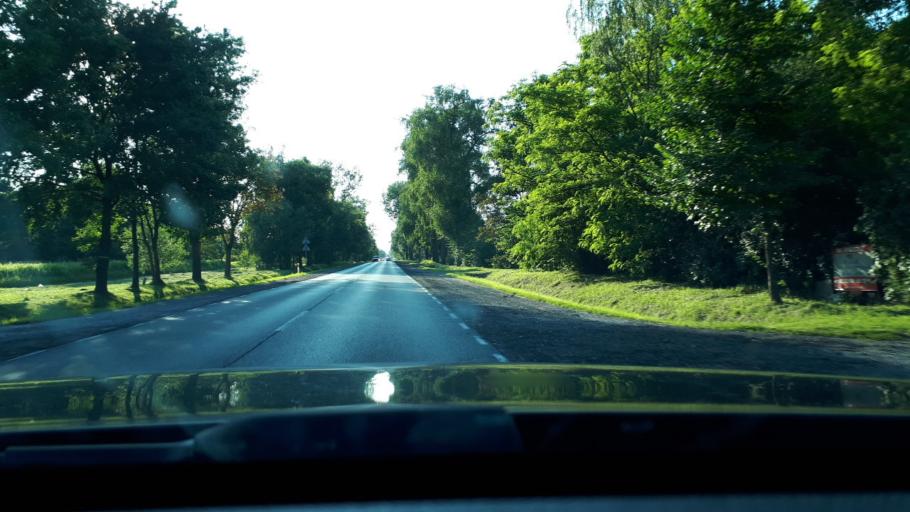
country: PL
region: Masovian Voivodeship
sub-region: Powiat piaseczynski
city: Baniocha
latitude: 52.0173
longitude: 21.1379
